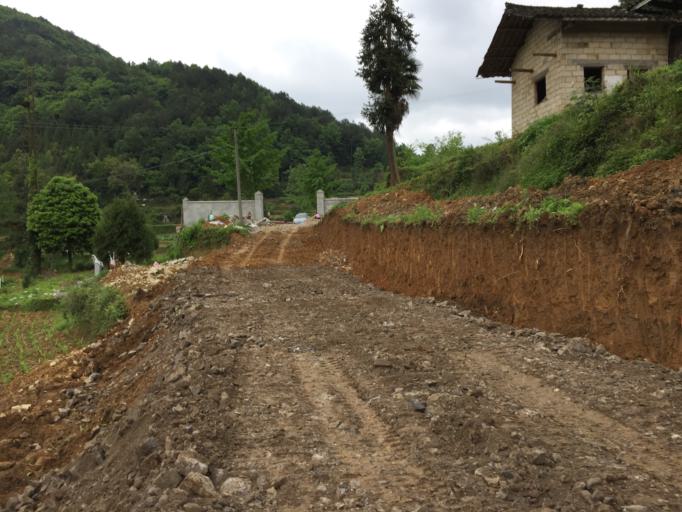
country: CN
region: Guizhou Sheng
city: Kuanping
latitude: 28.0096
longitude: 108.0669
